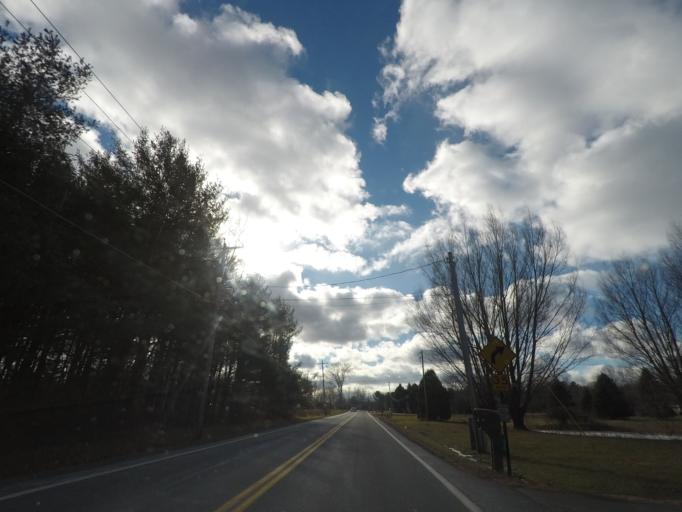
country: US
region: New York
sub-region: Schenectady County
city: East Glenville
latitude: 42.8875
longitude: -73.8798
